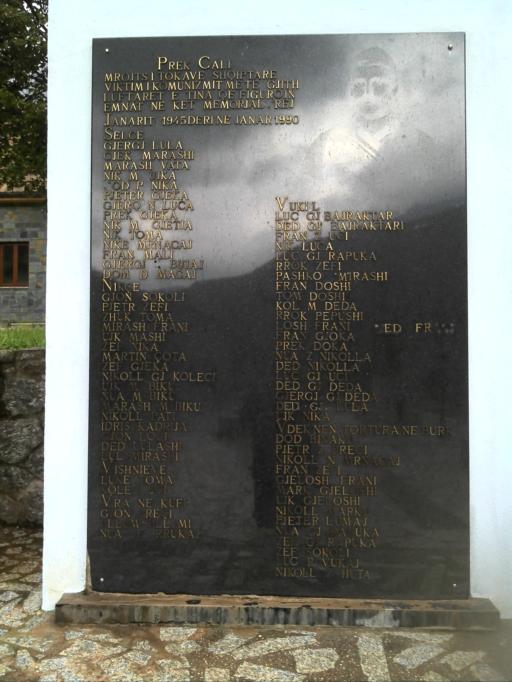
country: AL
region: Shkoder
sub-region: Rrethi i Malesia e Madhe
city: Kastrat
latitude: 42.4633
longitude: 19.5616
